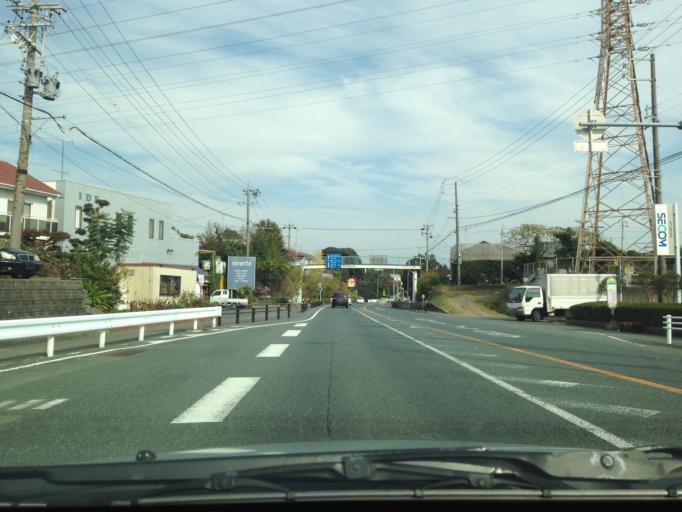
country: JP
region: Shizuoka
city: Iwata
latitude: 34.7299
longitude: 137.8700
